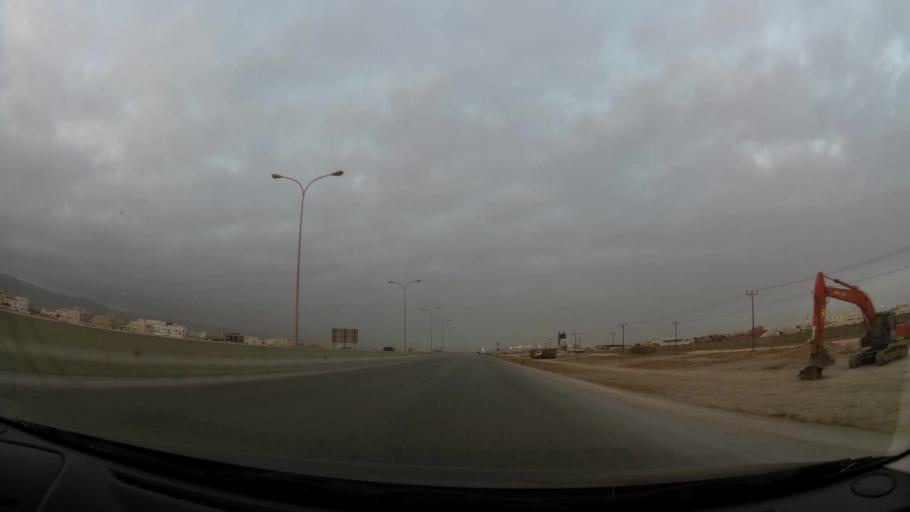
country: OM
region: Zufar
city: Salalah
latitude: 17.0327
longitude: 54.0322
